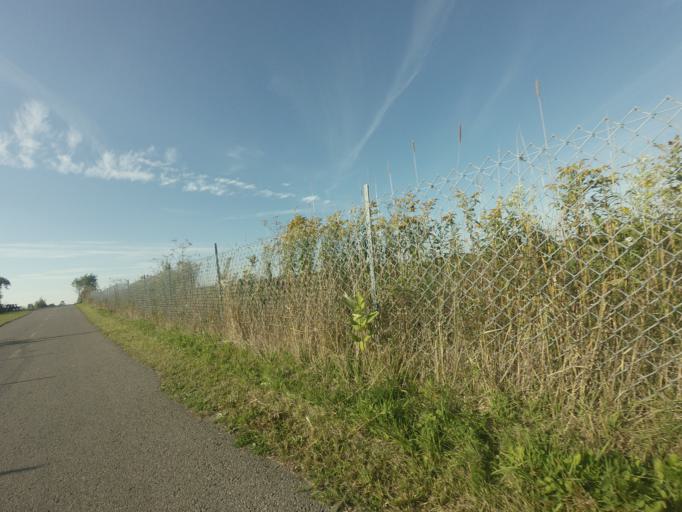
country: CA
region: Quebec
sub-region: Laurentides
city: Saint-Jerome
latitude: 45.7483
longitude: -73.9693
